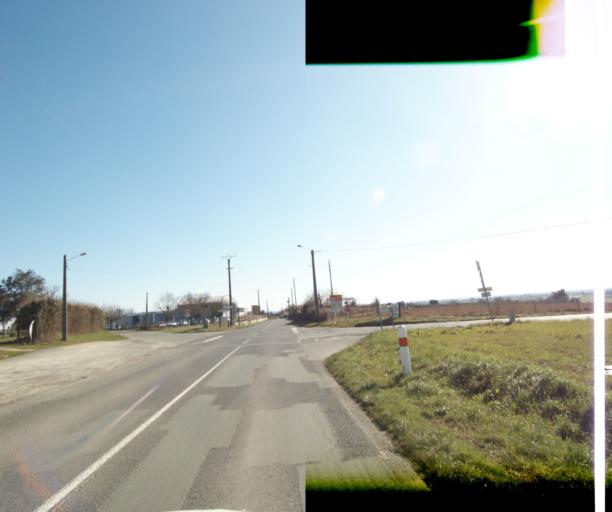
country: FR
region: Poitou-Charentes
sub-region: Departement des Deux-Sevres
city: Niort
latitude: 46.3563
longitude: -0.4814
